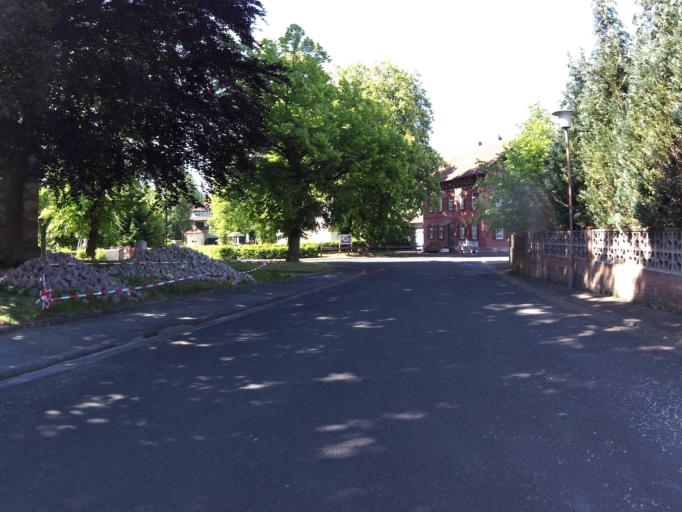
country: DE
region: Thuringia
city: Dankmarshausen
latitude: 50.9490
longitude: 10.0361
